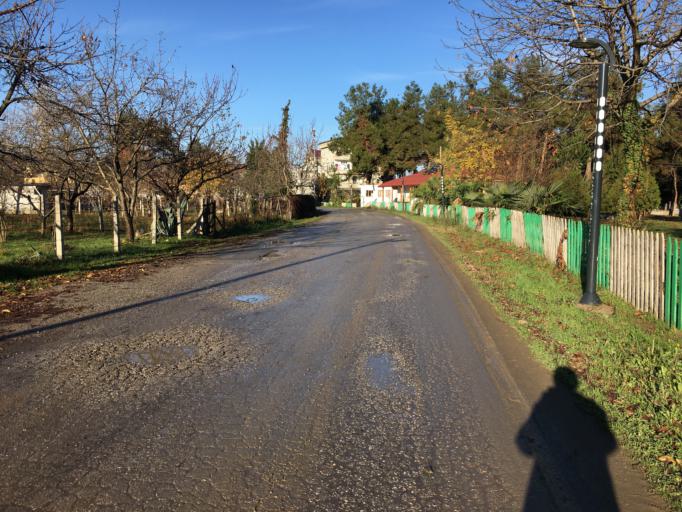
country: TR
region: Samsun
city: Alacam
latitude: 41.6133
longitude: 35.6036
